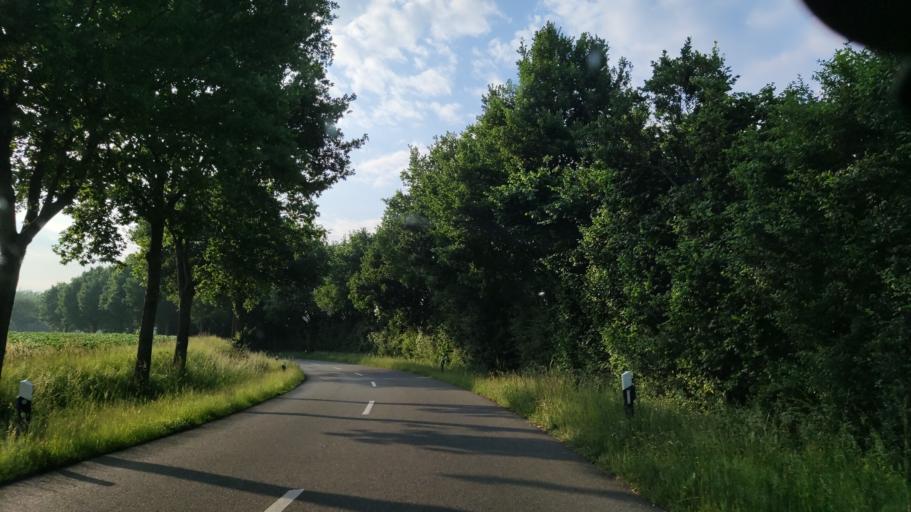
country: DE
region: Lower Saxony
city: Hanstedt Eins
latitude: 53.0309
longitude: 10.3543
